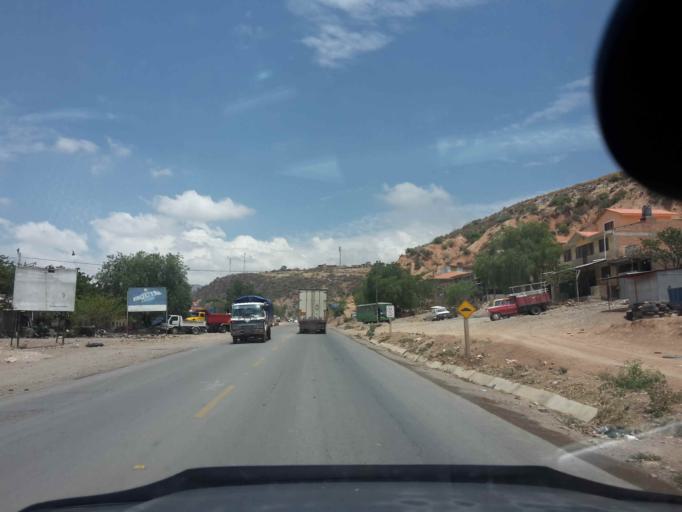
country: BO
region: Cochabamba
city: Sipe Sipe
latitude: -17.5634
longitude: -66.3445
